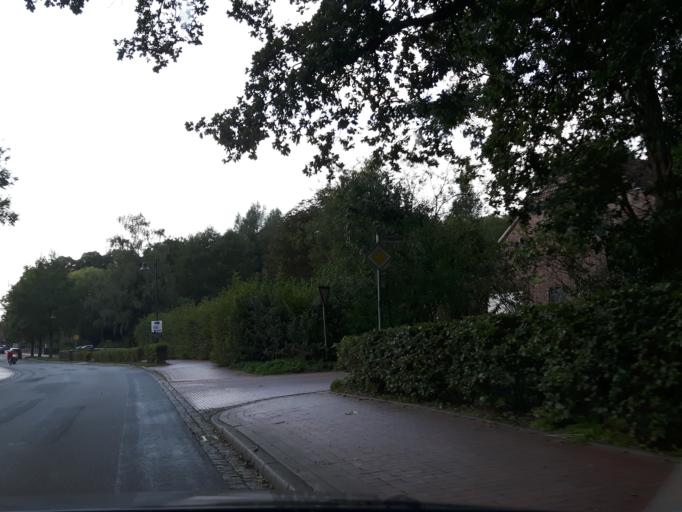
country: DE
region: Lower Saxony
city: Grossenkneten
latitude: 52.9913
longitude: 8.2844
